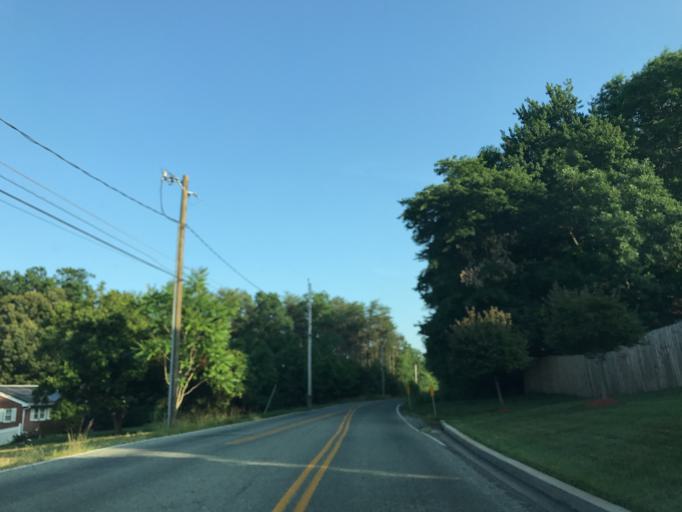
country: US
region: Maryland
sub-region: Harford County
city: Joppatowne
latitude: 39.4162
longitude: -76.3463
